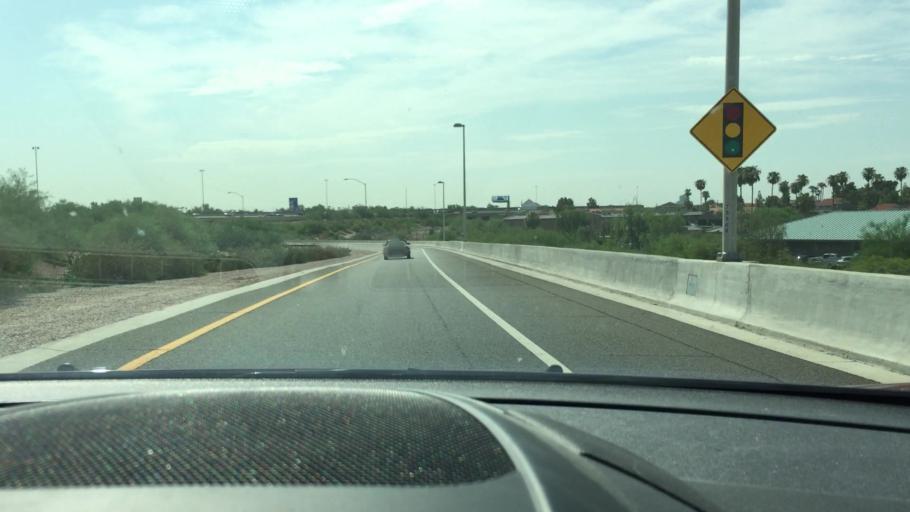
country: US
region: Arizona
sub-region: Maricopa County
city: Tempe Junction
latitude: 33.4555
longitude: -111.9745
